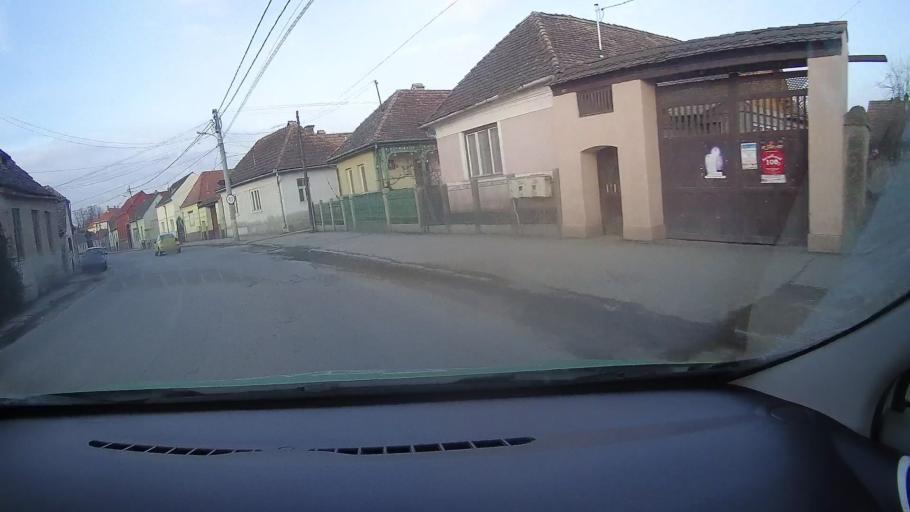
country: RO
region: Harghita
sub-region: Oras Cristuru Secuiesc
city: Cristuru Secuiesc
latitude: 46.2846
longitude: 25.0282
